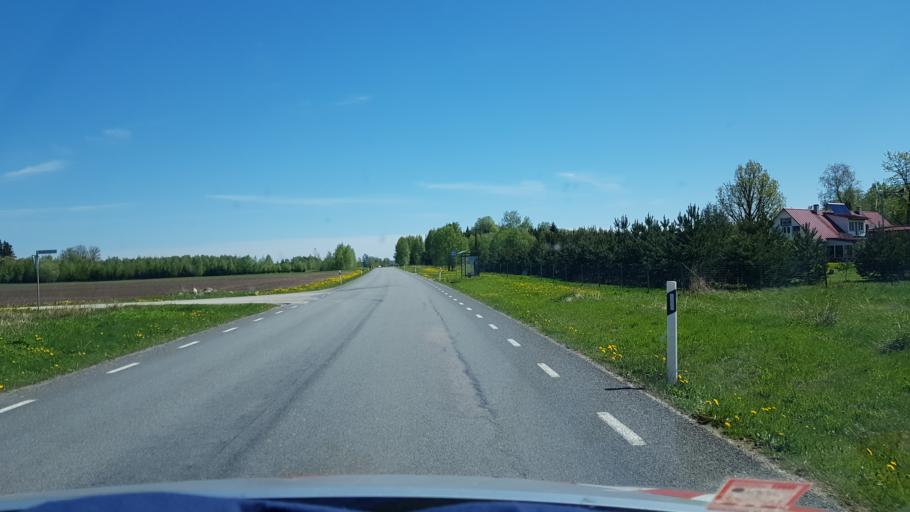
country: EE
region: Tartu
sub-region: UElenurme vald
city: Ulenurme
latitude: 58.3132
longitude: 26.6515
